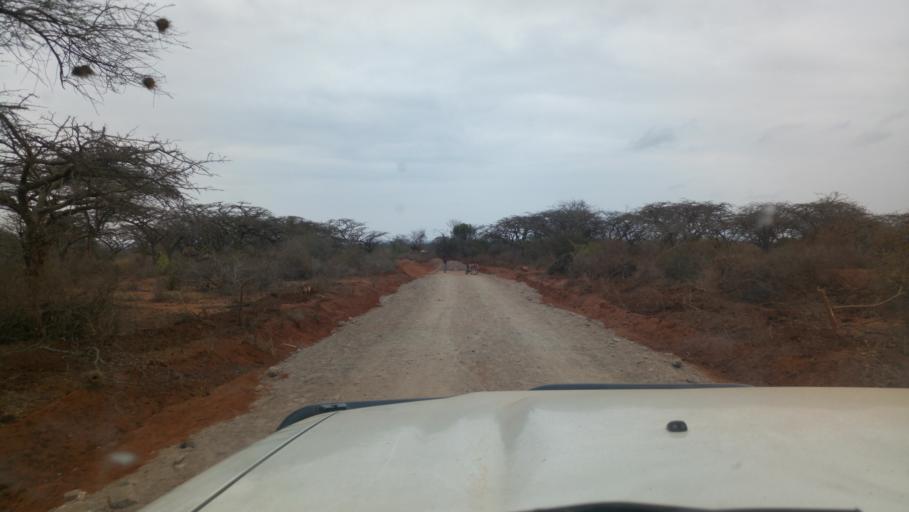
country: KE
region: Makueni
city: Wote
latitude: -1.8926
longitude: 38.1364
